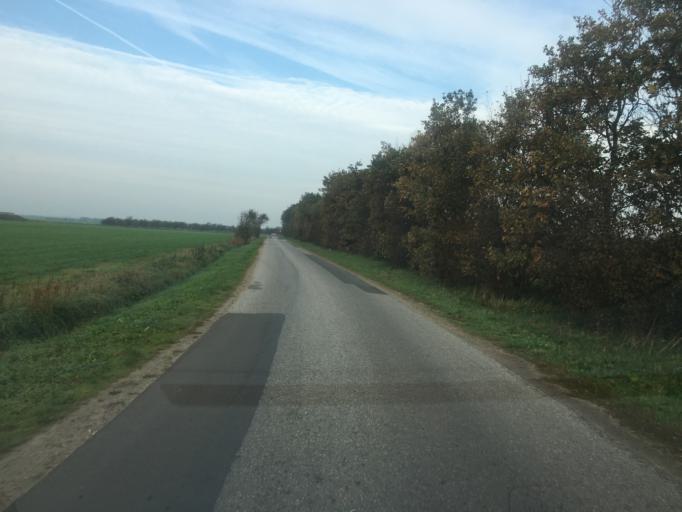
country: DK
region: South Denmark
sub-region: Tonder Kommune
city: Logumkloster
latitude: 55.0893
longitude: 9.0193
